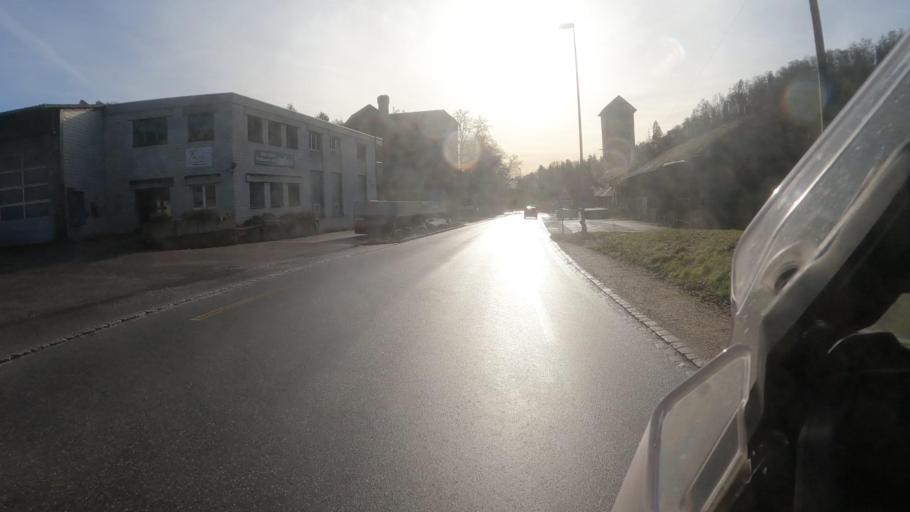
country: CH
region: Schaffhausen
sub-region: Bezirk Schaffhausen
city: Schaffhausen
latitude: 47.7253
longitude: 8.6304
